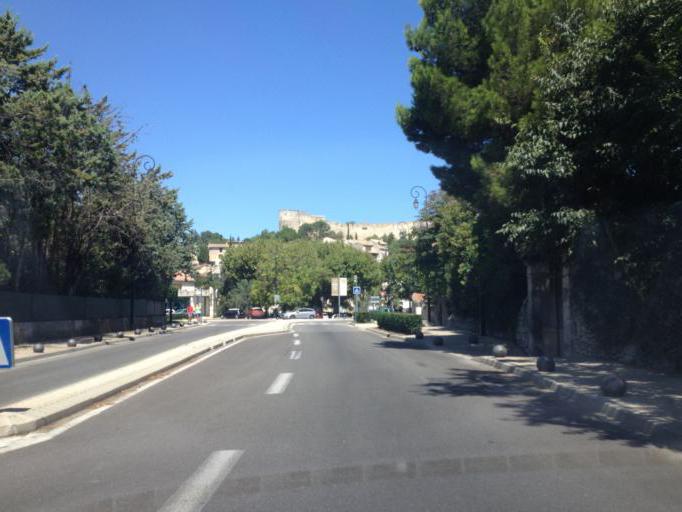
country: FR
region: Languedoc-Roussillon
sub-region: Departement du Gard
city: Villeneuve-les-Avignon
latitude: 43.9623
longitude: 4.7995
